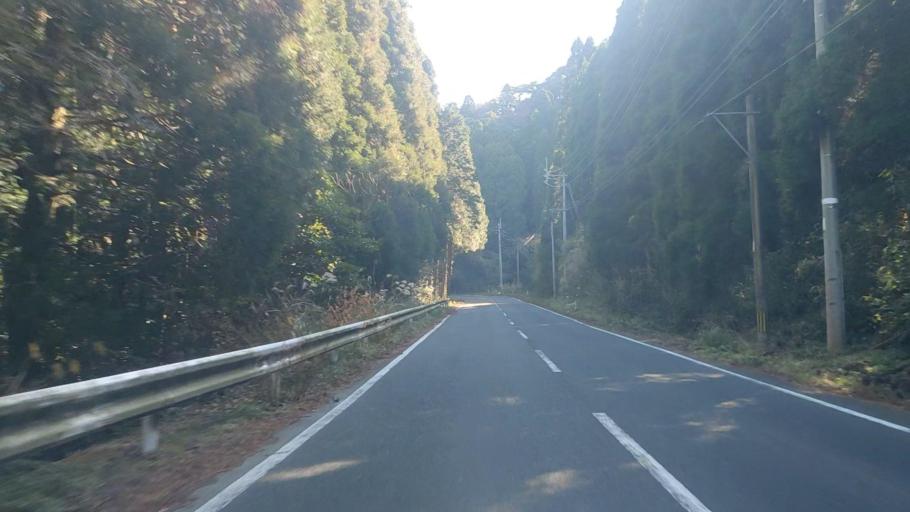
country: JP
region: Kagoshima
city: Kokubu-matsuki
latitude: 31.6700
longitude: 130.8358
